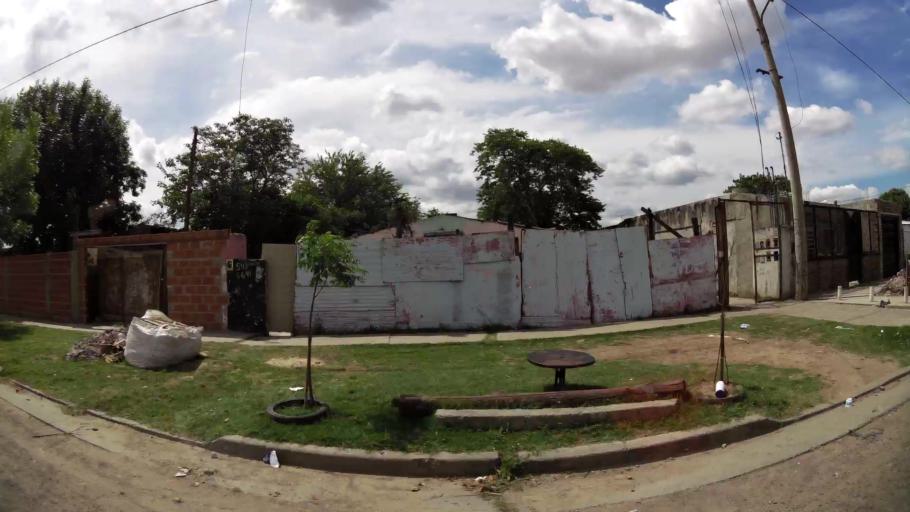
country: AR
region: Santa Fe
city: Gobernador Galvez
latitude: -33.0156
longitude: -60.6398
